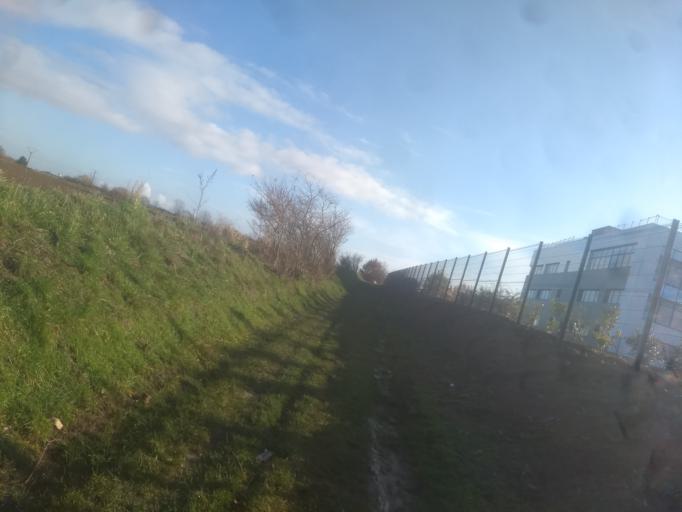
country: FR
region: Nord-Pas-de-Calais
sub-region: Departement du Pas-de-Calais
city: Anzin-Saint-Aubin
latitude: 50.3068
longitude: 2.7302
